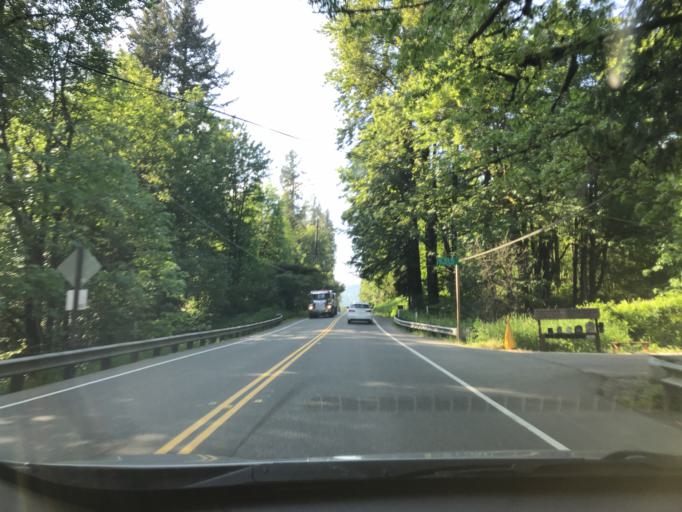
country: US
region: Washington
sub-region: King County
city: Mirrormont
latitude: 47.4632
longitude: -122.0137
